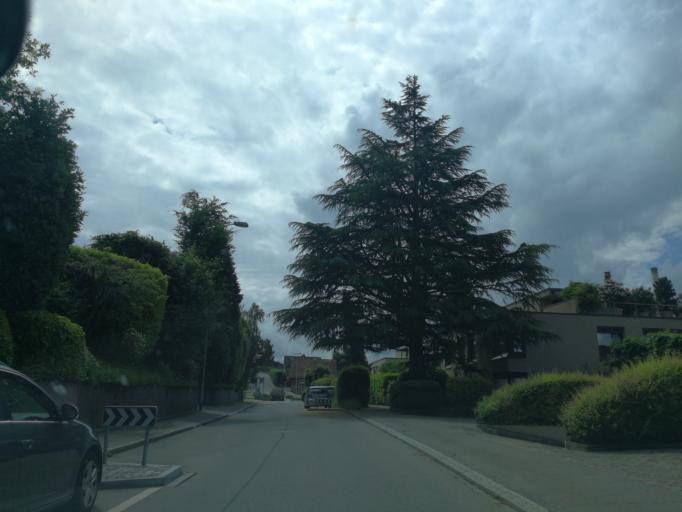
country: CH
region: Zurich
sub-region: Bezirk Meilen
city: Erlenbach / links des Dorfbachs oberhalb Bahnlinie
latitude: 47.2964
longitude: 8.6037
